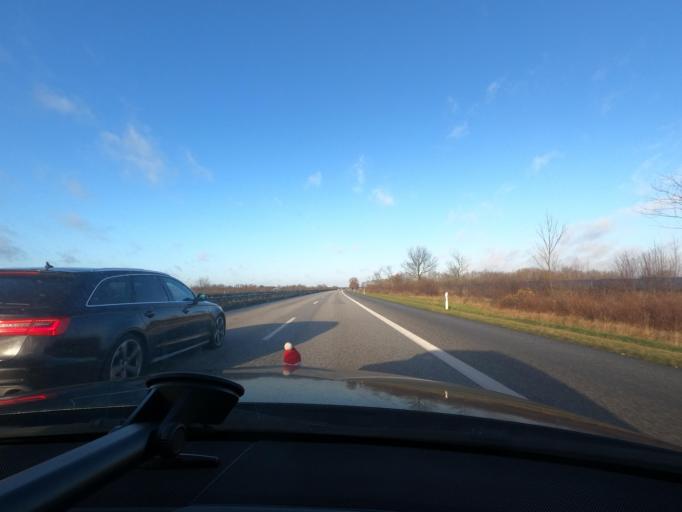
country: DE
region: Schleswig-Holstein
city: Sankelmark
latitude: 54.7073
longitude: 9.4013
